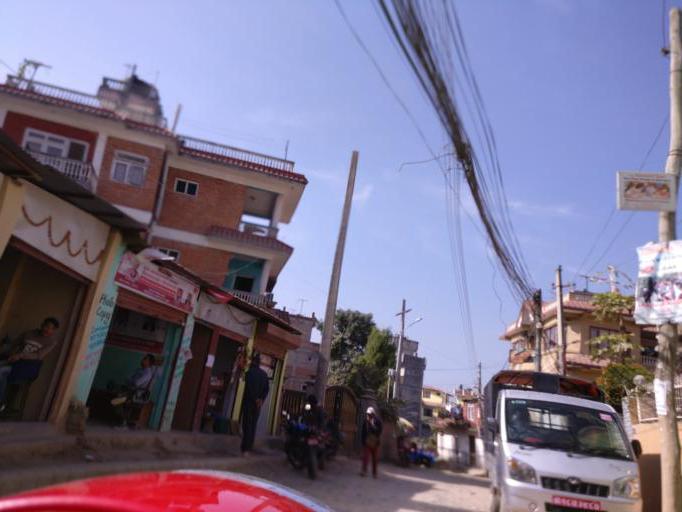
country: NP
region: Central Region
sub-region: Bagmati Zone
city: Patan
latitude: 27.6642
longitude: 85.3107
